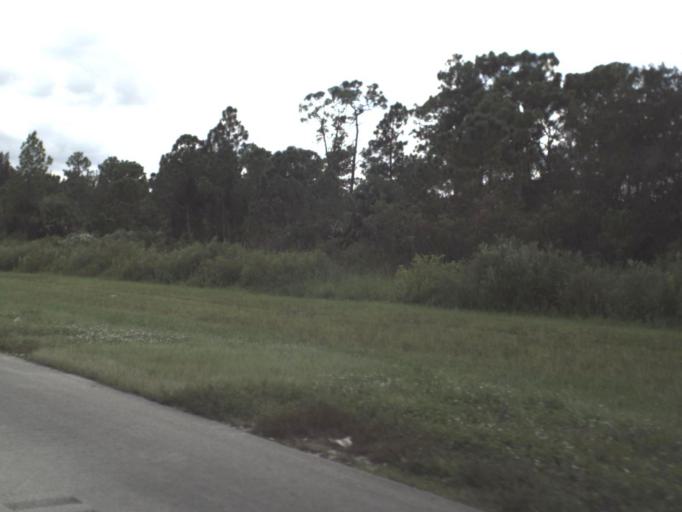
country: US
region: Florida
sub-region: Martin County
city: Palm City
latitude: 27.1234
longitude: -80.2790
